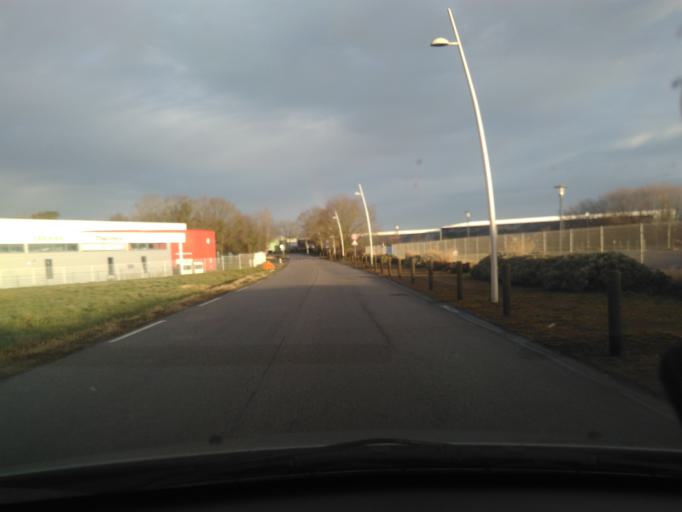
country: FR
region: Pays de la Loire
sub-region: Departement de la Vendee
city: Dompierre-sur-Yon
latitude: 46.6972
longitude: -1.3721
